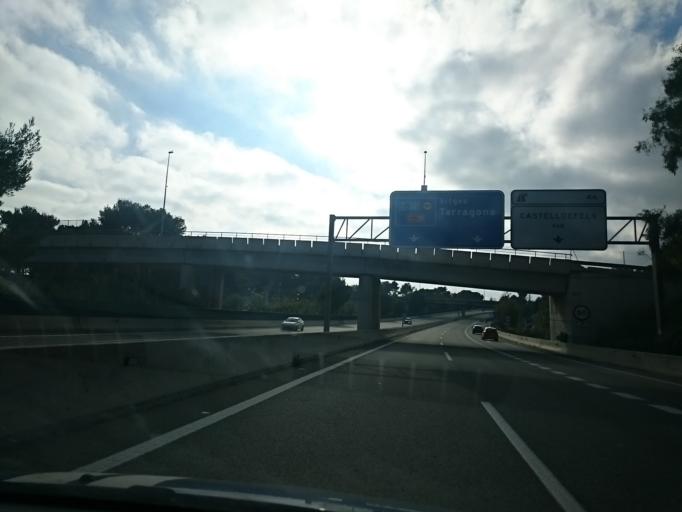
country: ES
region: Catalonia
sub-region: Provincia de Barcelona
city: Castelldefels
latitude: 41.2706
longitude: 1.9685
